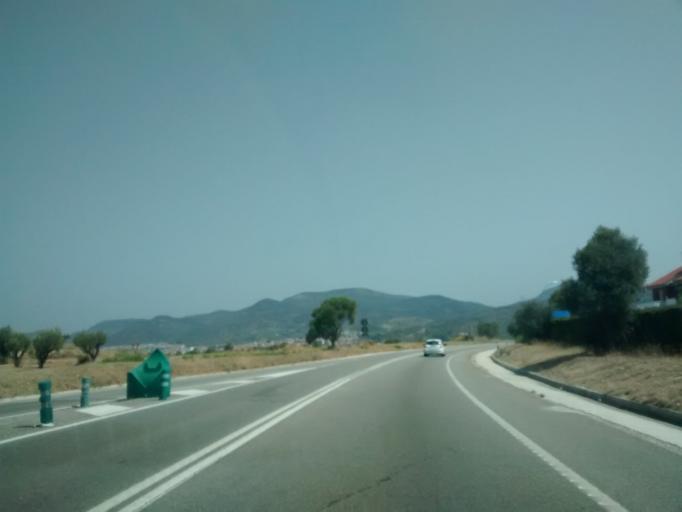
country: ES
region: Catalonia
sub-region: Provincia de Barcelona
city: Abrera
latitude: 41.5216
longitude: 1.8981
